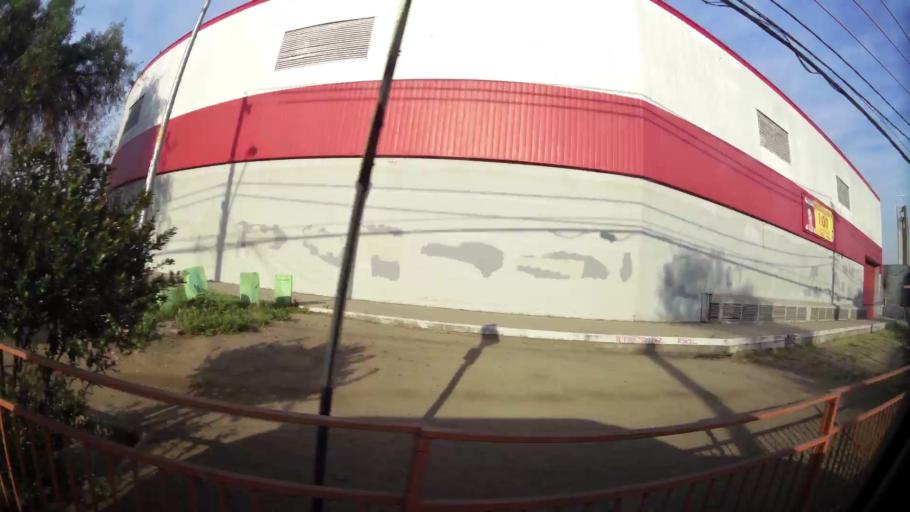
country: CL
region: Santiago Metropolitan
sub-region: Provincia de Maipo
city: San Bernardo
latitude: -33.5603
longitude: -70.7866
